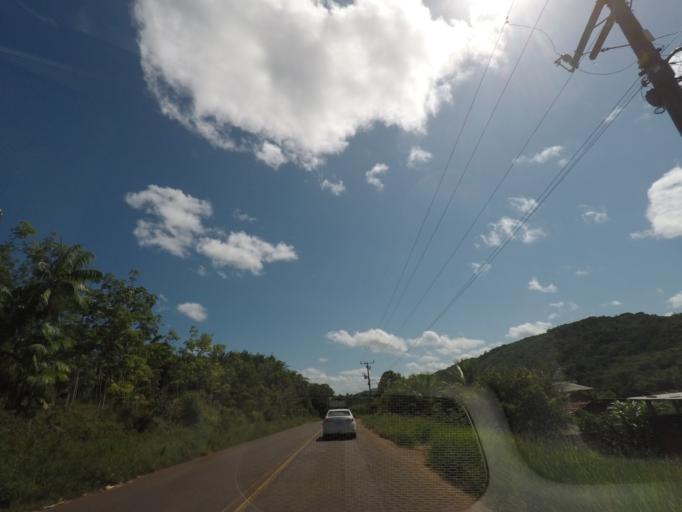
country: BR
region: Bahia
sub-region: Itubera
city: Itubera
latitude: -13.6774
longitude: -39.1252
